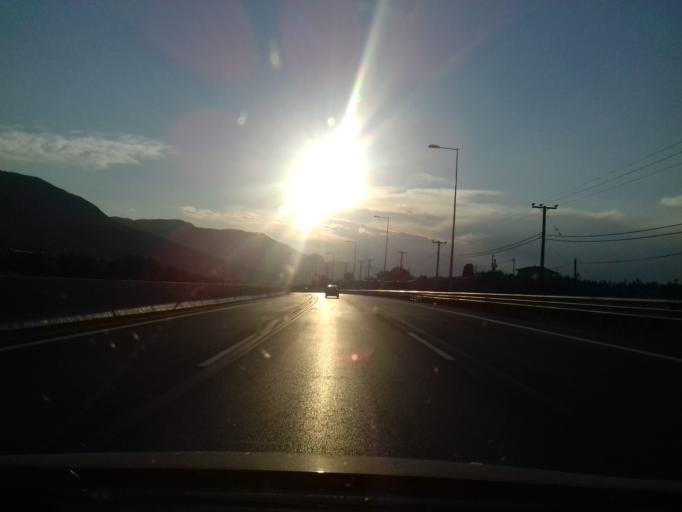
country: GR
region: West Greece
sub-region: Nomos Achaias
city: Akrata
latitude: 38.1716
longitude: 22.2945
